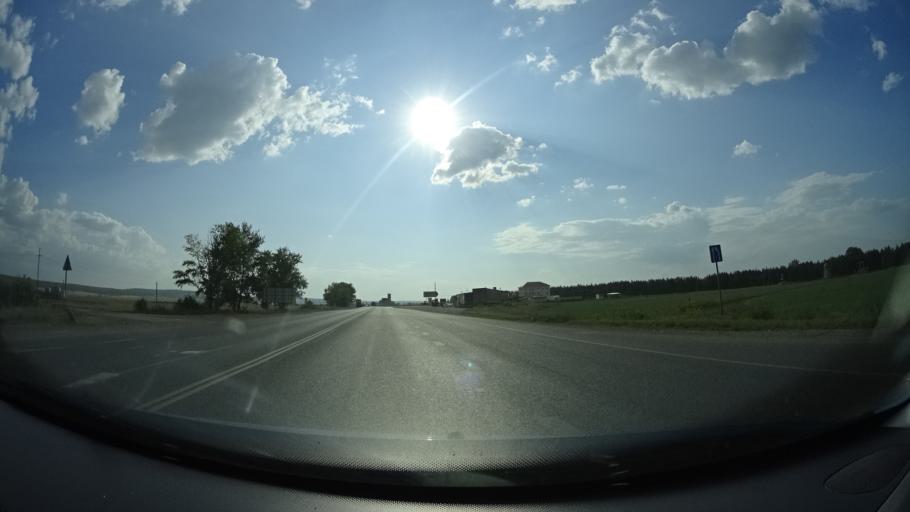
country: RU
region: Bashkortostan
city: Oktyabr'skiy
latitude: 54.4792
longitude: 53.3546
